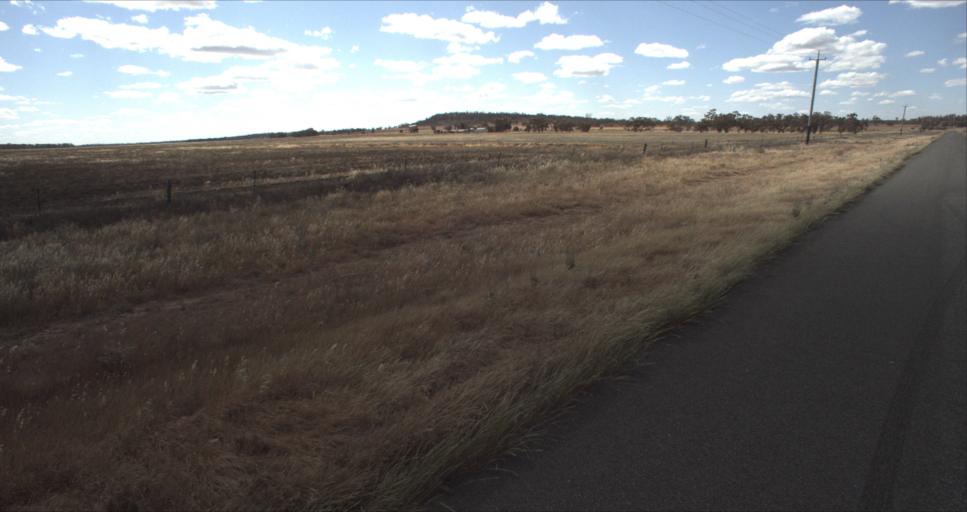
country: AU
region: New South Wales
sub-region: Leeton
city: Leeton
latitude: -34.4329
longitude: 146.2579
